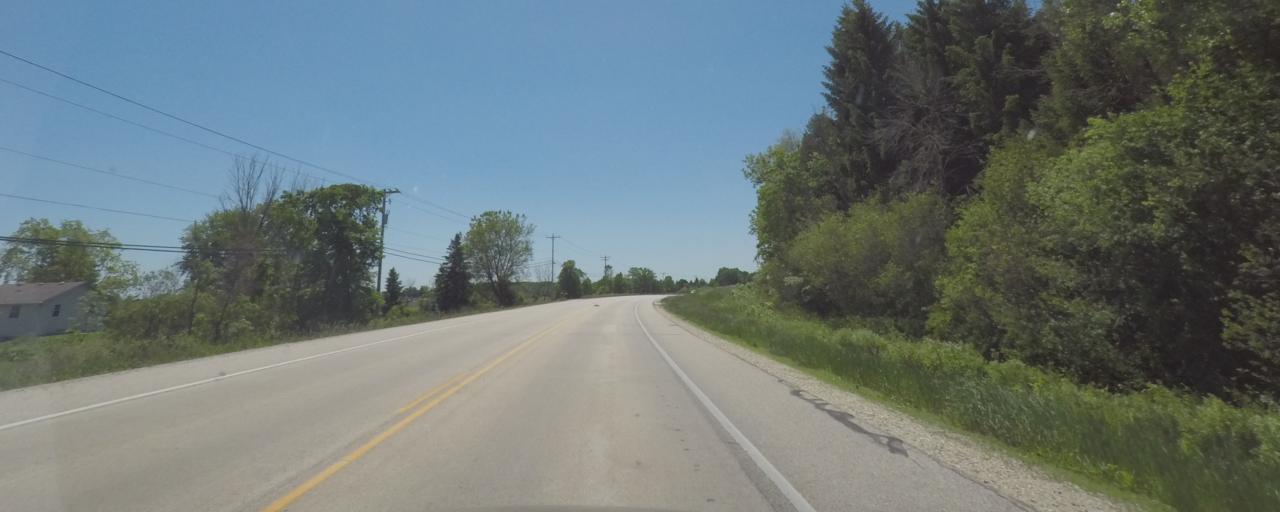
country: US
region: Wisconsin
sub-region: Washington County
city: West Bend
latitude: 43.4796
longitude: -88.1410
